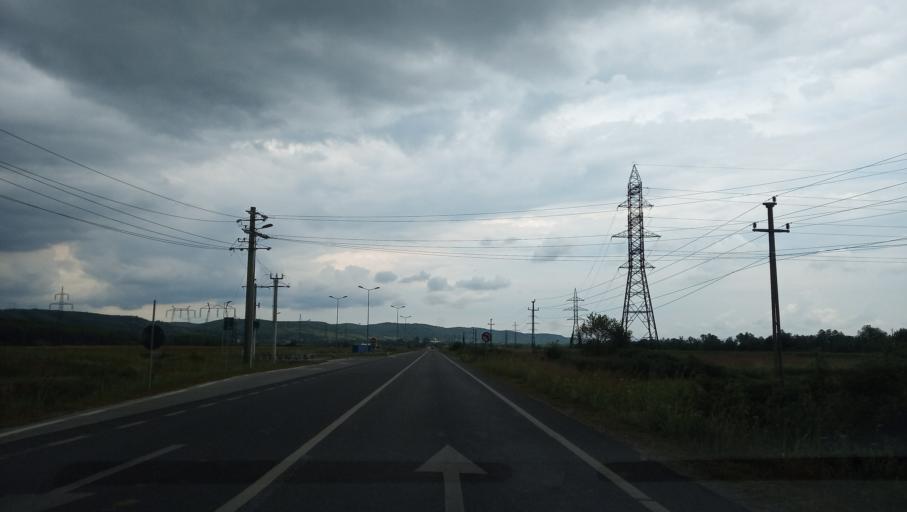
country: RO
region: Gorj
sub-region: Oras Rovinari
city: Rovinari
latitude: 44.9011
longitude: 23.1759
